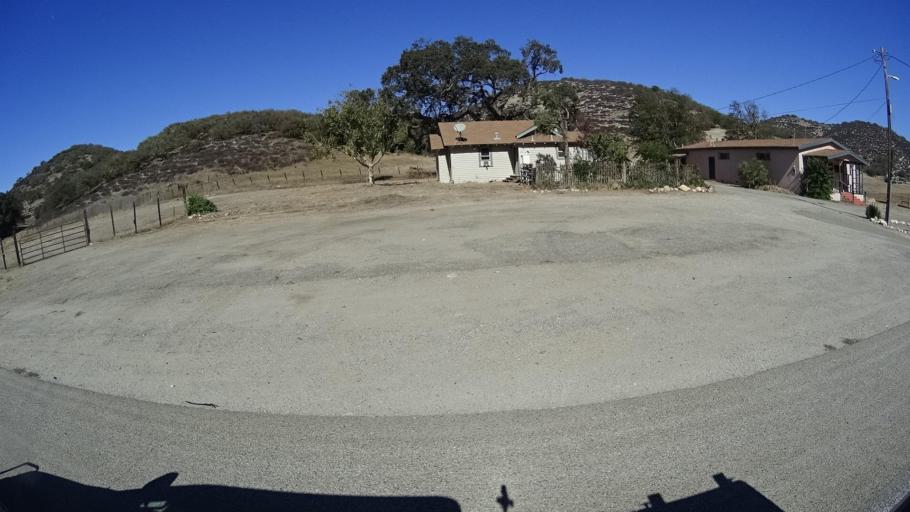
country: US
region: California
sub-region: Monterey County
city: King City
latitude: 36.1070
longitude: -121.1362
